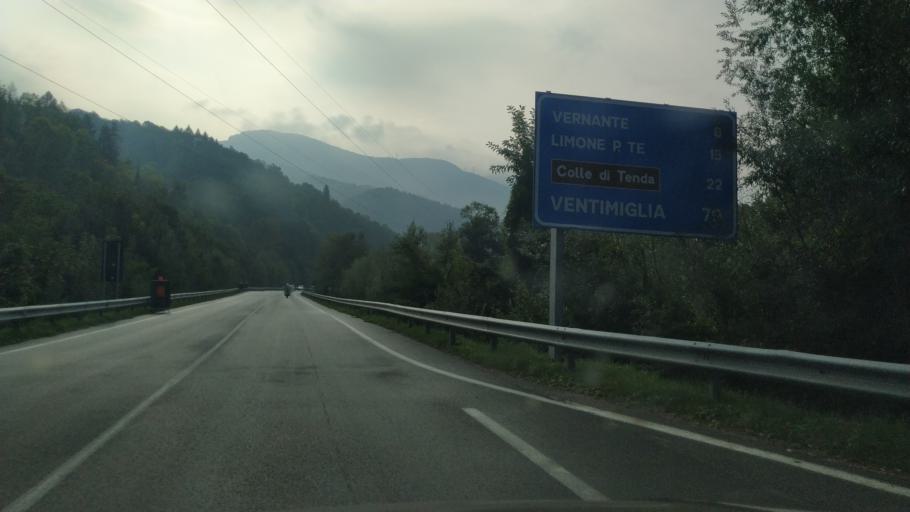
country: IT
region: Piedmont
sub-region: Provincia di Cuneo
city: Robilante
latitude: 44.3042
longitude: 7.5111
